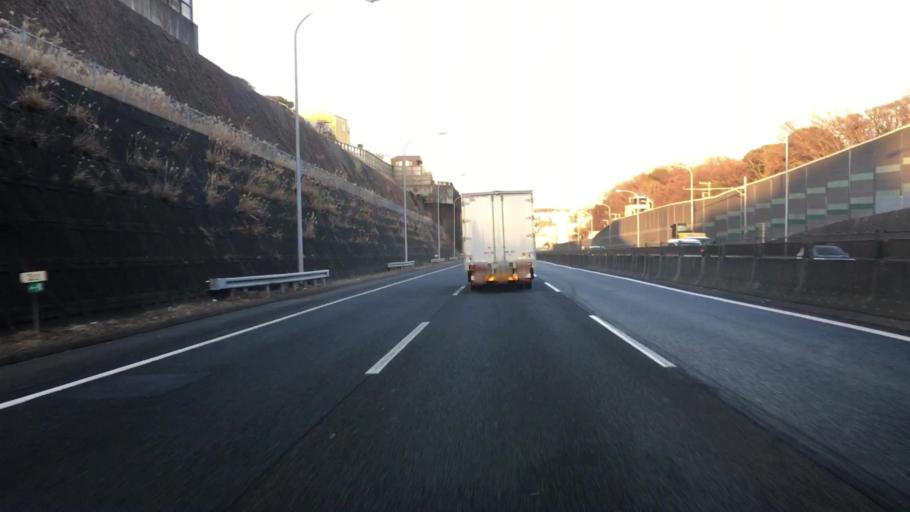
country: JP
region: Kanagawa
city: Yokohama
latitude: 35.4564
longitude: 139.5827
